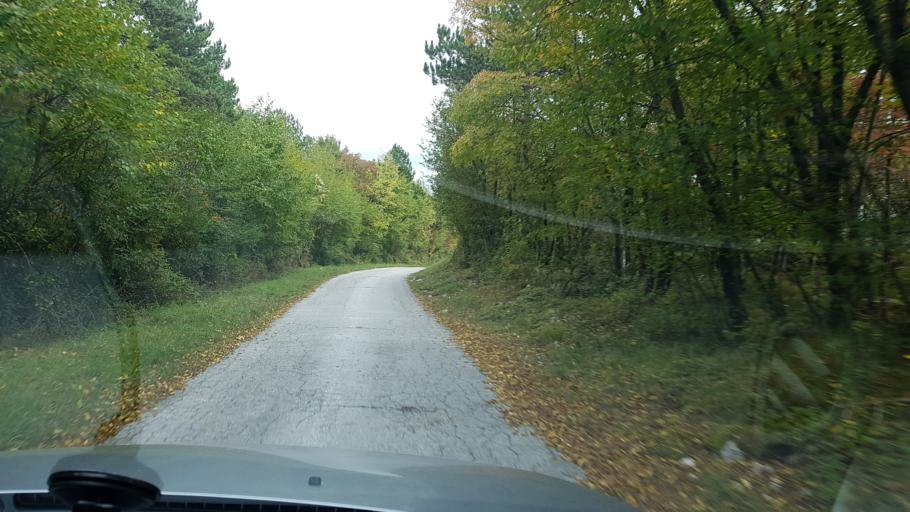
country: HR
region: Istarska
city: Buzet
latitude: 45.4481
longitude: 14.0286
